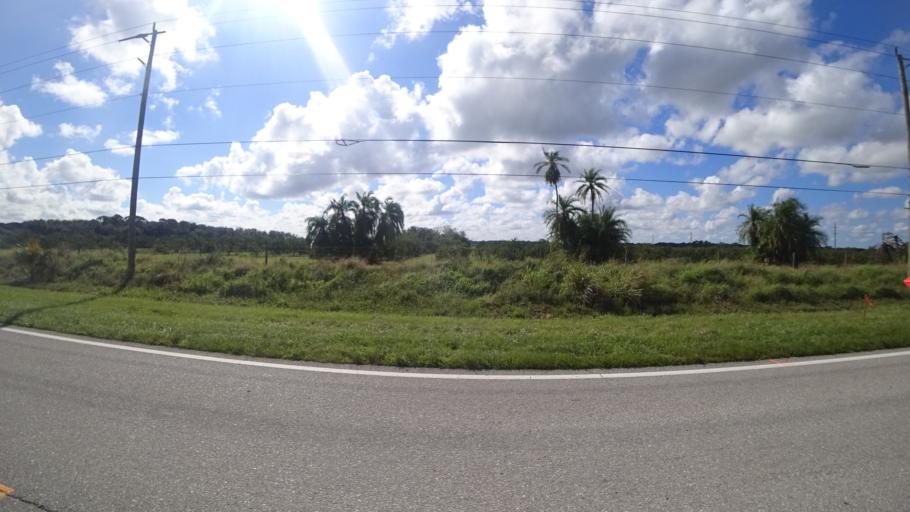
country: US
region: Florida
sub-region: Manatee County
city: Ellenton
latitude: 27.6012
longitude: -82.4767
